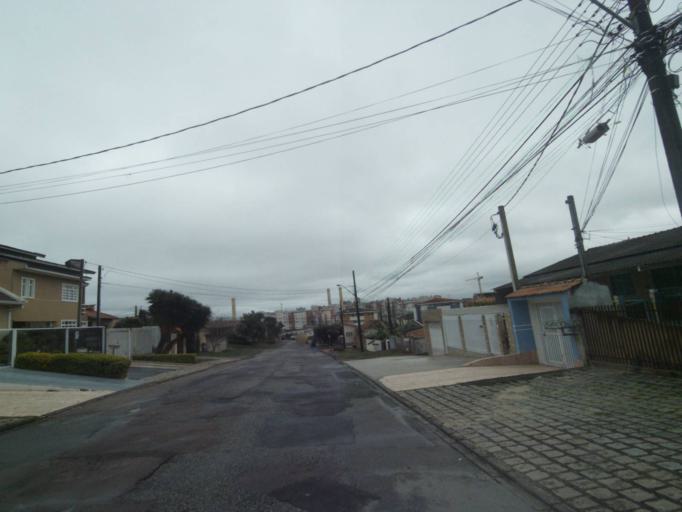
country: BR
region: Parana
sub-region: Curitiba
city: Curitiba
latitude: -25.5033
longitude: -49.3050
